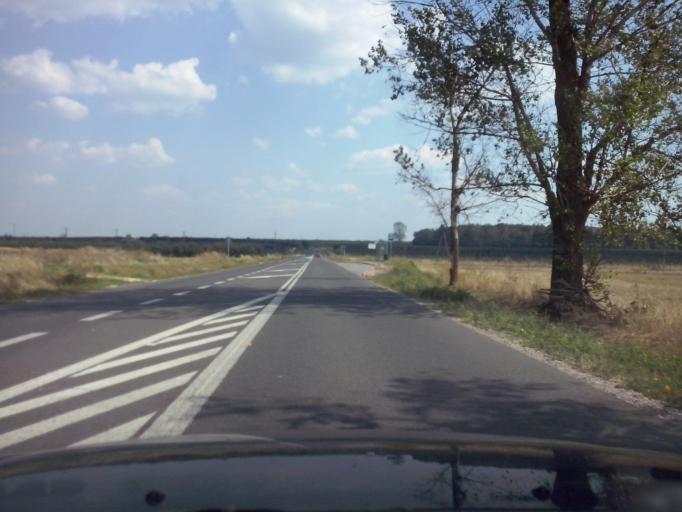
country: PL
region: Swietokrzyskie
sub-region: Powiat staszowski
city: Szydlow
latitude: 50.5850
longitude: 21.0483
